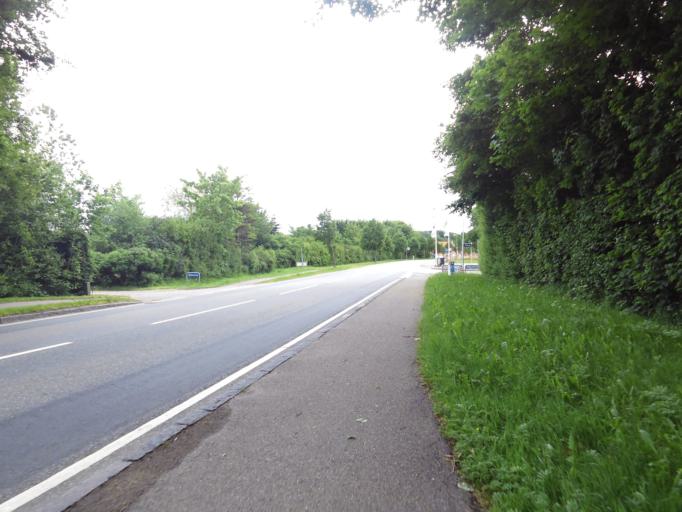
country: DK
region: South Denmark
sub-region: Haderslev Kommune
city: Gram
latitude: 55.2993
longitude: 9.0598
